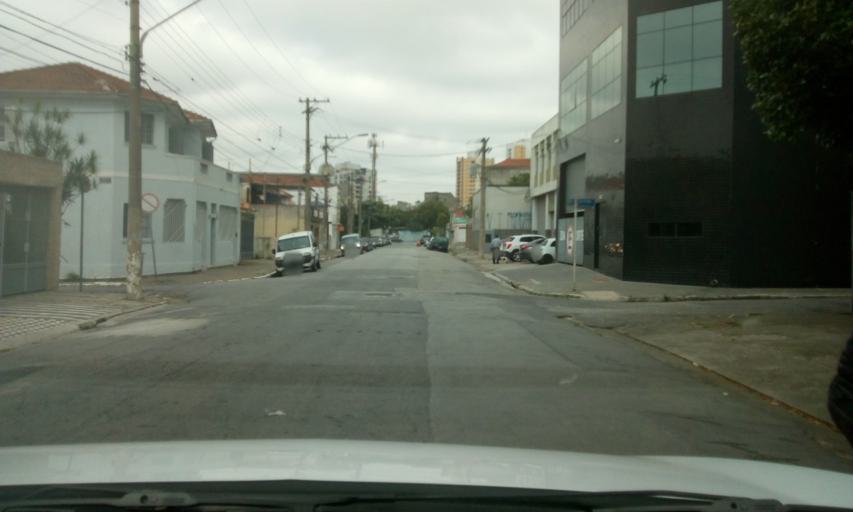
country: BR
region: Sao Paulo
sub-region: Sao Paulo
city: Sao Paulo
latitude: -23.5232
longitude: -46.6146
